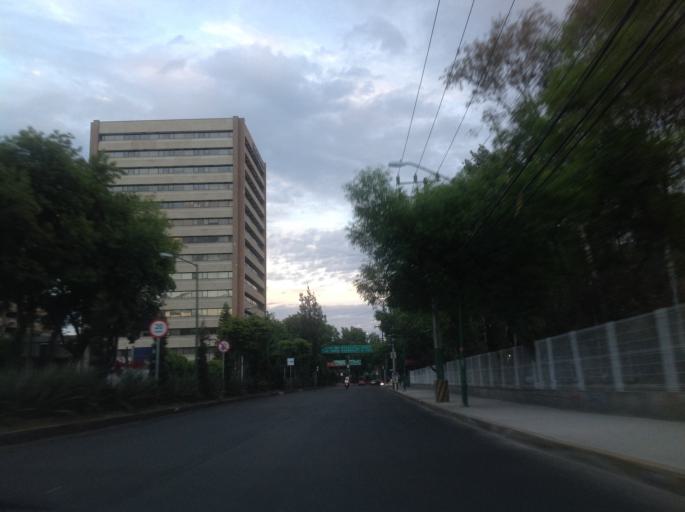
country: MX
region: Mexico City
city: Magdalena Contreras
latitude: 19.3109
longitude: -99.2225
